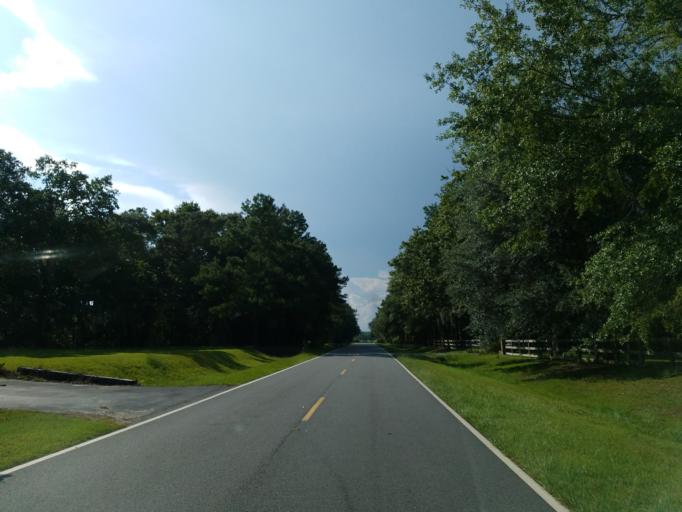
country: US
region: Georgia
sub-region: Lowndes County
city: Hahira
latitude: 31.0248
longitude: -83.4381
